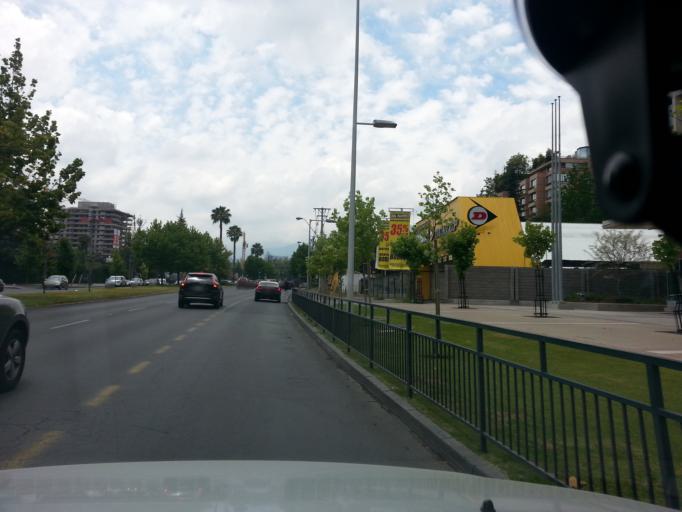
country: CL
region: Santiago Metropolitan
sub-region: Provincia de Santiago
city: Villa Presidente Frei, Nunoa, Santiago, Chile
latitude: -33.3771
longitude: -70.5270
